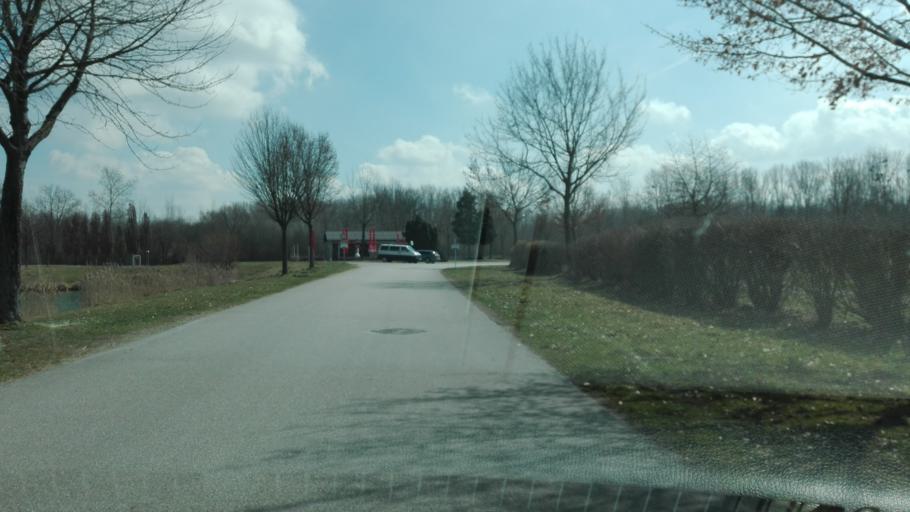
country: AT
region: Upper Austria
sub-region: Politischer Bezirk Urfahr-Umgebung
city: Goldworth
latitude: 48.3250
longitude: 14.0736
